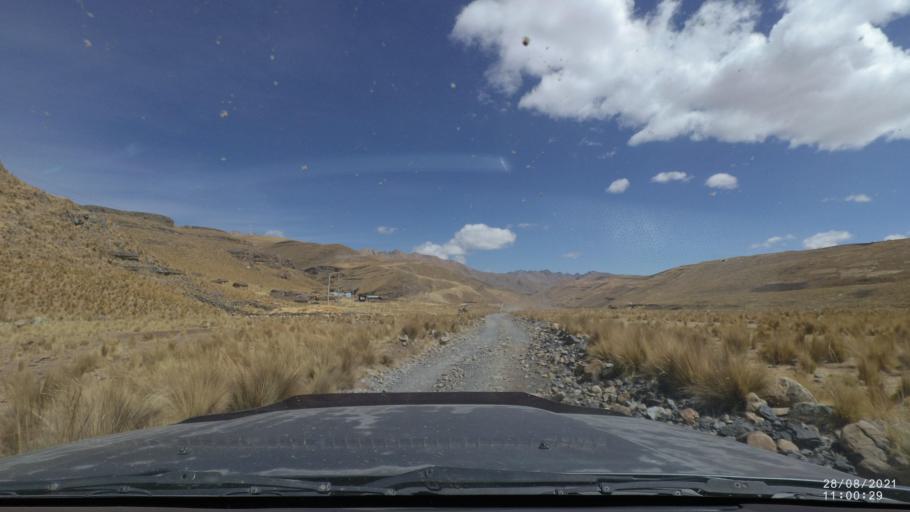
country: BO
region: Cochabamba
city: Cochabamba
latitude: -17.1830
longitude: -66.2606
